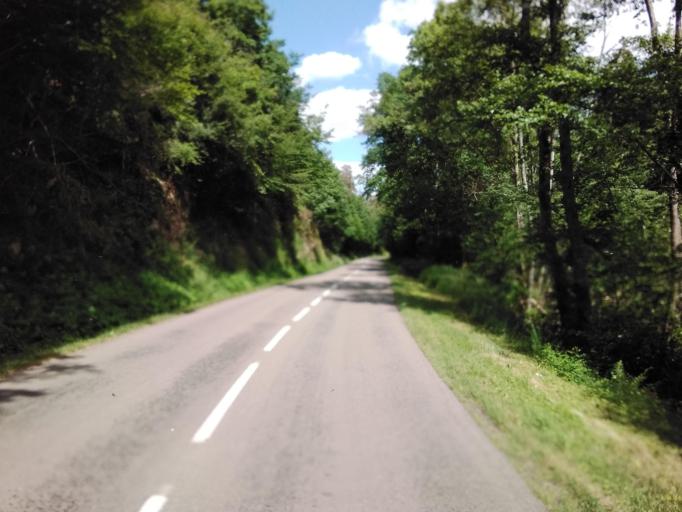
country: FR
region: Bourgogne
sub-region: Departement de l'Yonne
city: Avallon
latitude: 47.4675
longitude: 3.9030
